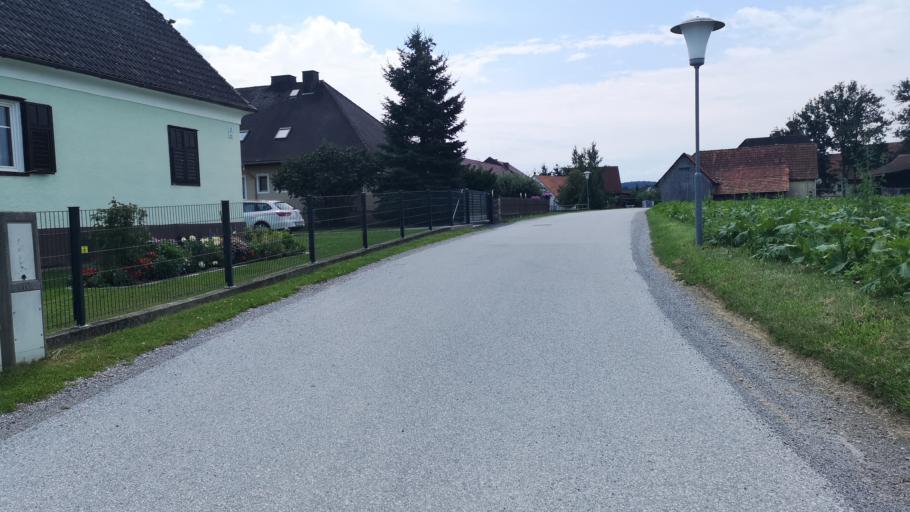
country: AT
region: Styria
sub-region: Politischer Bezirk Leibnitz
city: Weitendorf
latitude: 46.8996
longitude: 15.4763
